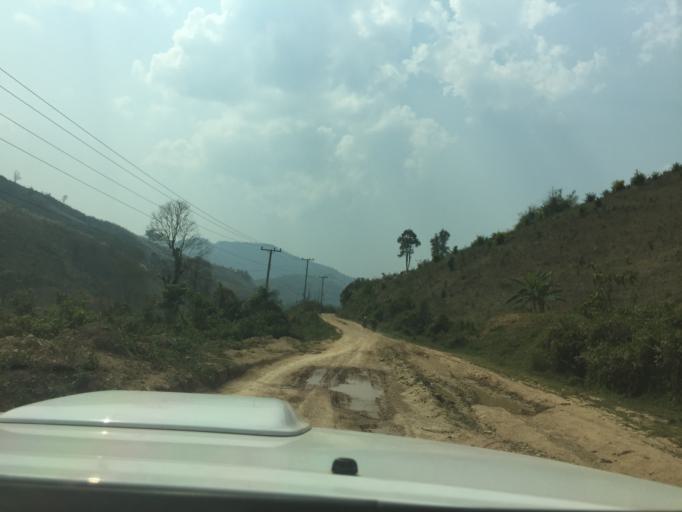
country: TH
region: Nan
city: Thung Chang
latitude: 19.7285
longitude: 100.7459
